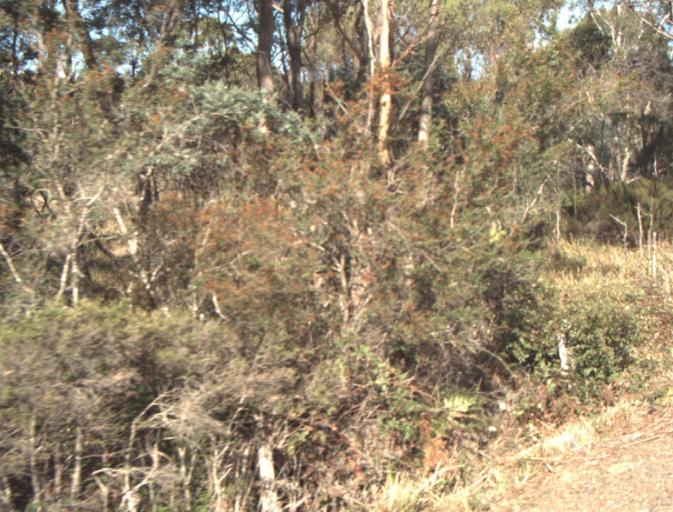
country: AU
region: Tasmania
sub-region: Launceston
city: Mayfield
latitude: -41.3289
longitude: 147.1401
